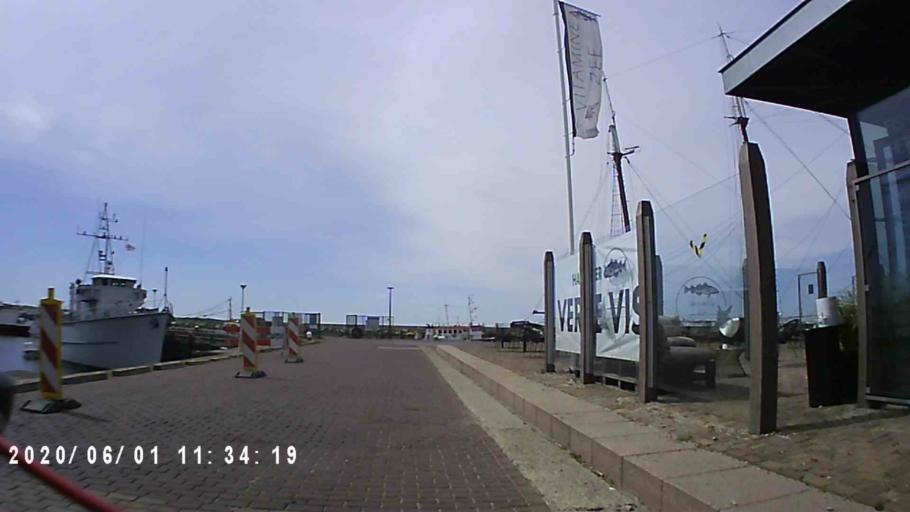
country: NL
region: Friesland
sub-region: Gemeente Harlingen
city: Harlingen
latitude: 53.1711
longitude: 5.4132
